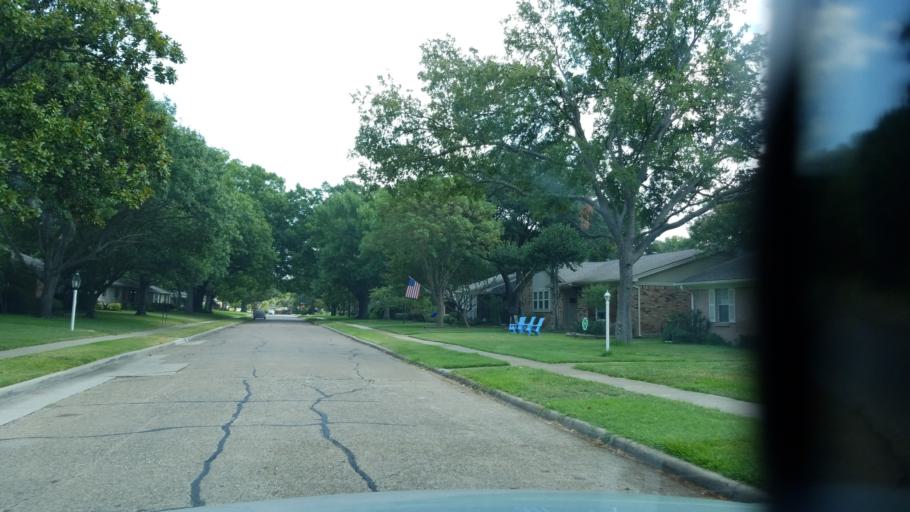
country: US
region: Texas
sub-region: Dallas County
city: Richardson
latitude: 32.9646
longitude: -96.7644
